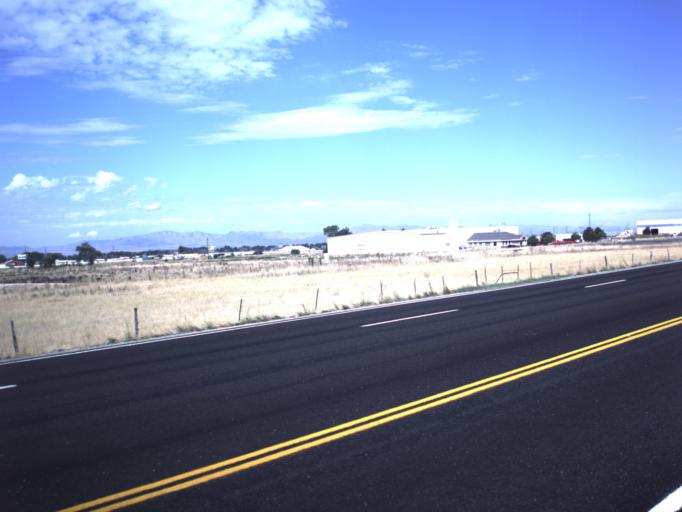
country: US
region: Utah
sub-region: Weber County
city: Pleasant View
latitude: 41.3220
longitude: -112.0172
